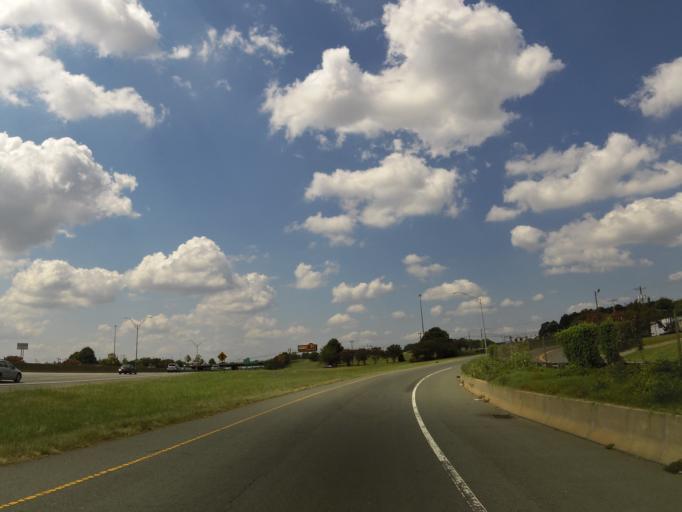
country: US
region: North Carolina
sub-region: Mecklenburg County
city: Charlotte
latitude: 35.2773
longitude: -80.8054
